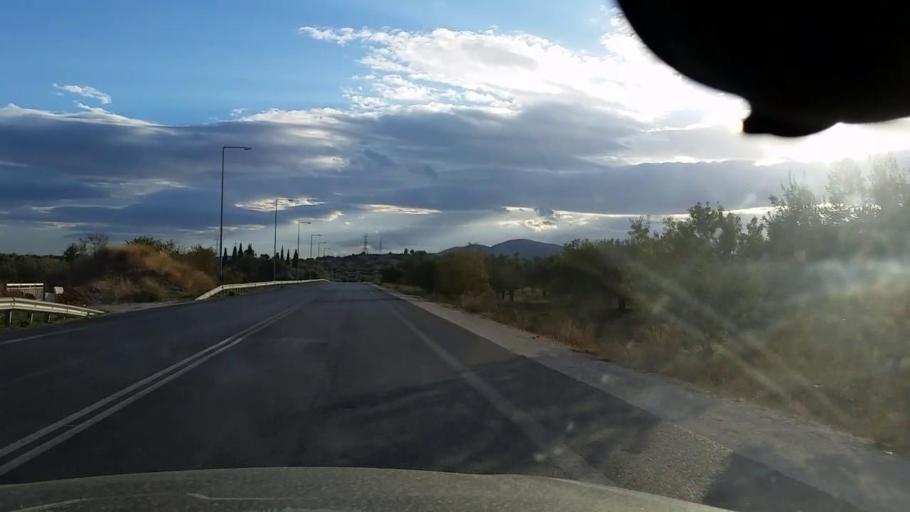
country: GR
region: Attica
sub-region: Nomarchia Anatolikis Attikis
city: Argithea
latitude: 37.9612
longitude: 23.8965
